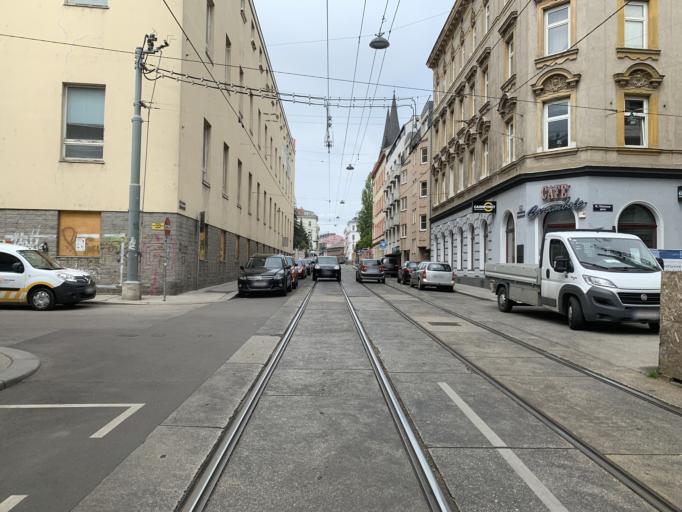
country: AT
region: Vienna
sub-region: Wien Stadt
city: Vienna
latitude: 48.2245
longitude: 16.3355
